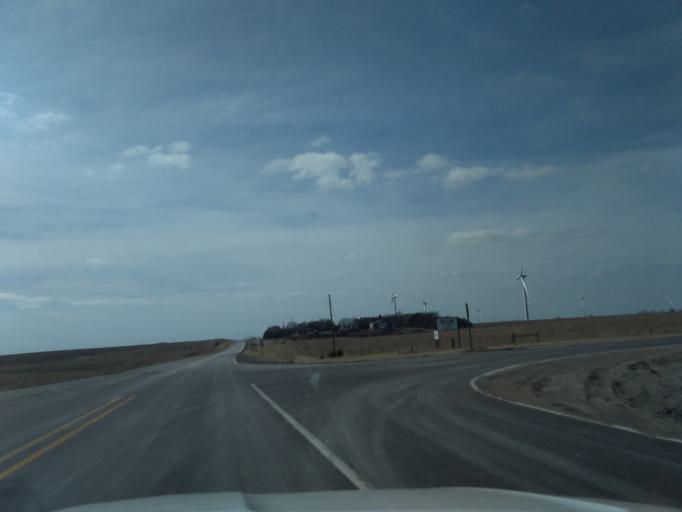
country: US
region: Kansas
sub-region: Washington County
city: Washington
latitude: 40.0448
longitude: -96.9346
